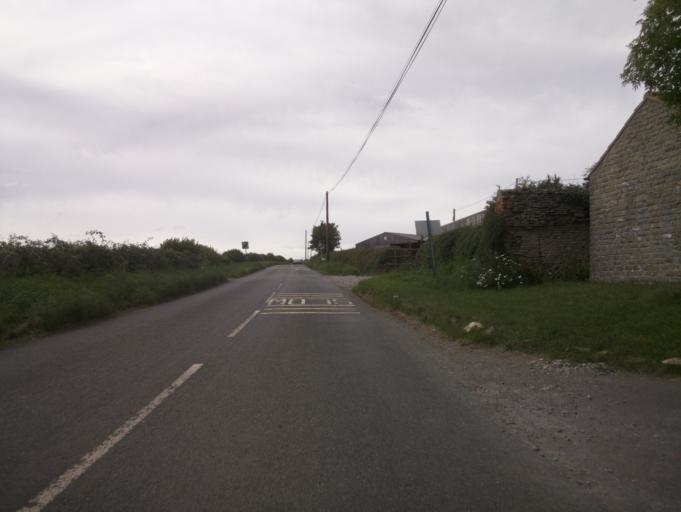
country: GB
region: England
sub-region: Somerset
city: Ilchester
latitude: 51.0627
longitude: -2.6774
